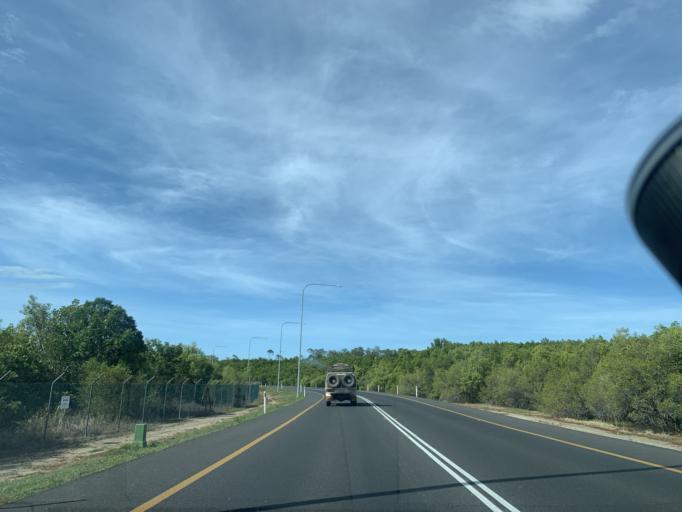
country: AU
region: Queensland
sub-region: Cairns
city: Cairns
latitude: -16.8887
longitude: 145.7619
